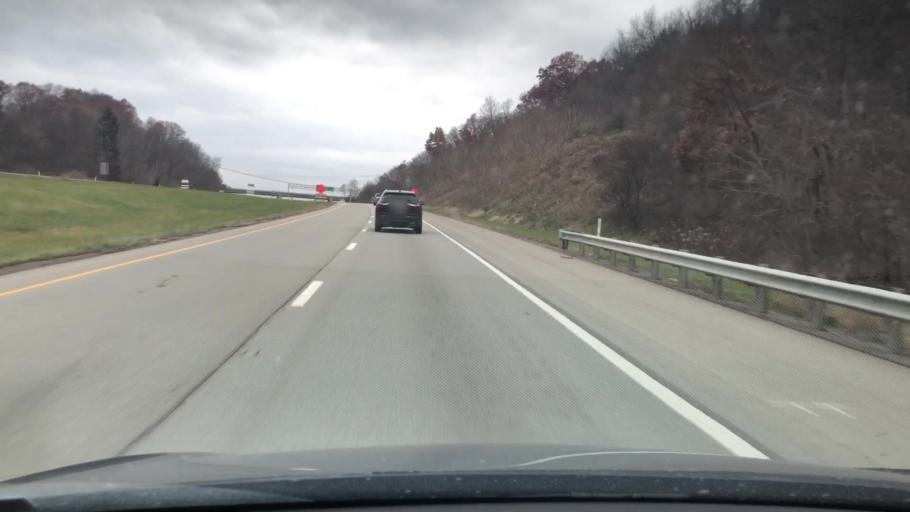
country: US
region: Pennsylvania
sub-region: Armstrong County
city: West Kittanning
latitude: 40.8072
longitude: -79.5408
